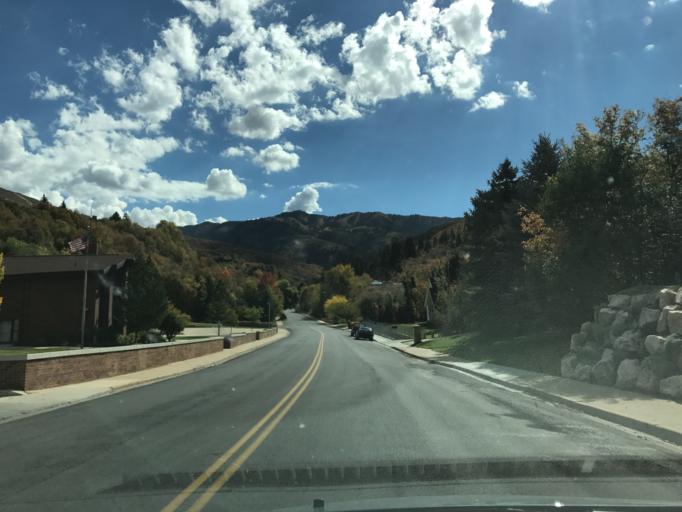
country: US
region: Utah
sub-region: Davis County
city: Bountiful
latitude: 40.8669
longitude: -111.8439
